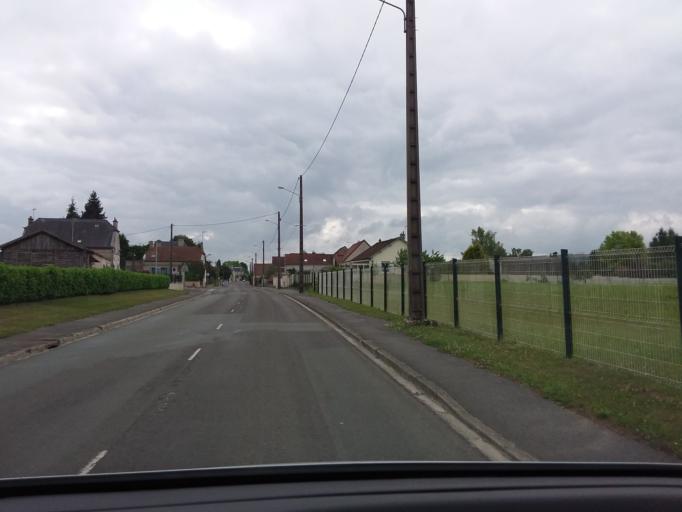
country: FR
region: Picardie
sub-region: Departement de l'Aisne
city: Vailly-sur-Aisne
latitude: 49.4085
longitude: 3.5101
